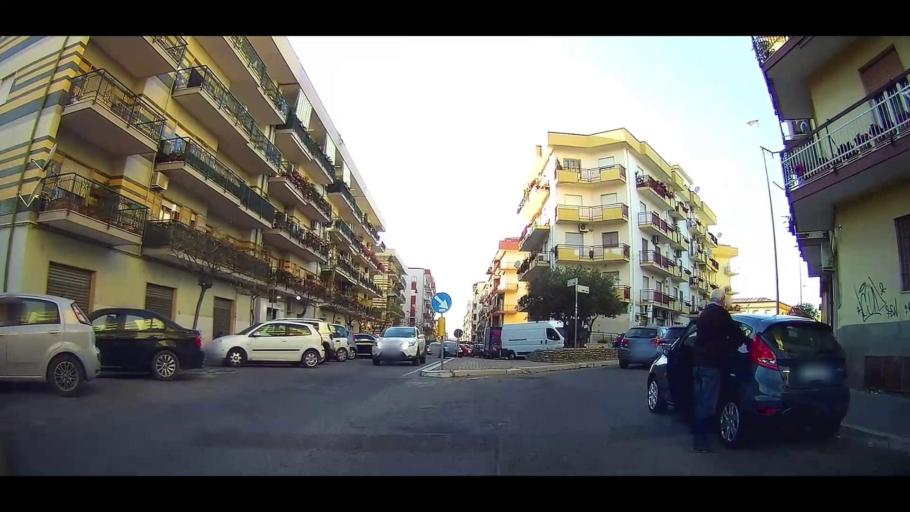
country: IT
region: Calabria
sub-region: Provincia di Crotone
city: Crotone
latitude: 39.0763
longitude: 17.1282
